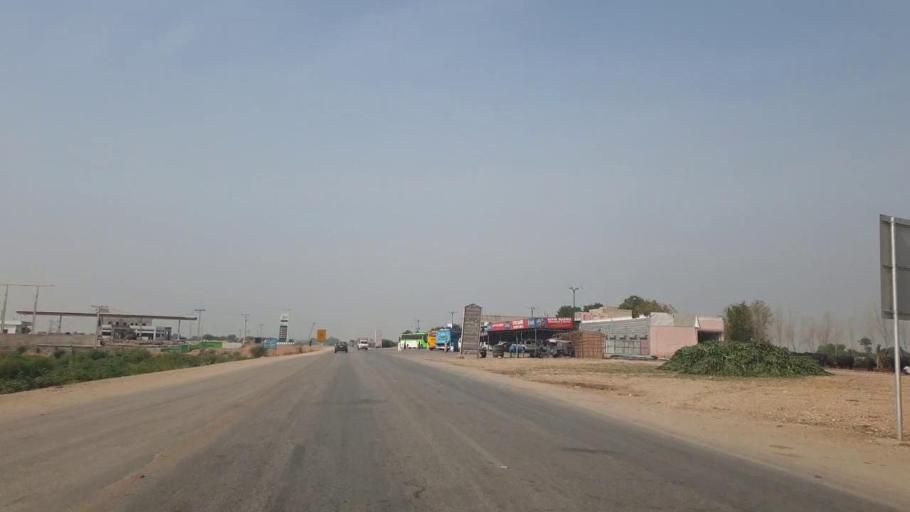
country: PK
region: Sindh
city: Sann
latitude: 26.1590
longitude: 68.0219
